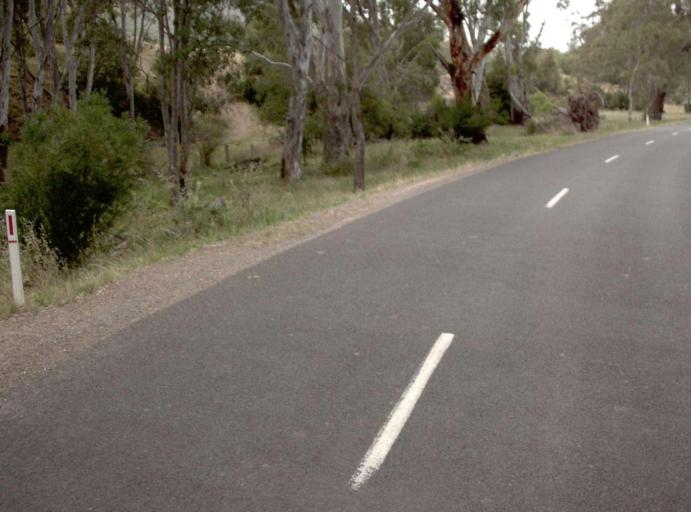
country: AU
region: Victoria
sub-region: Wellington
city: Heyfield
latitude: -37.6428
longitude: 146.6391
